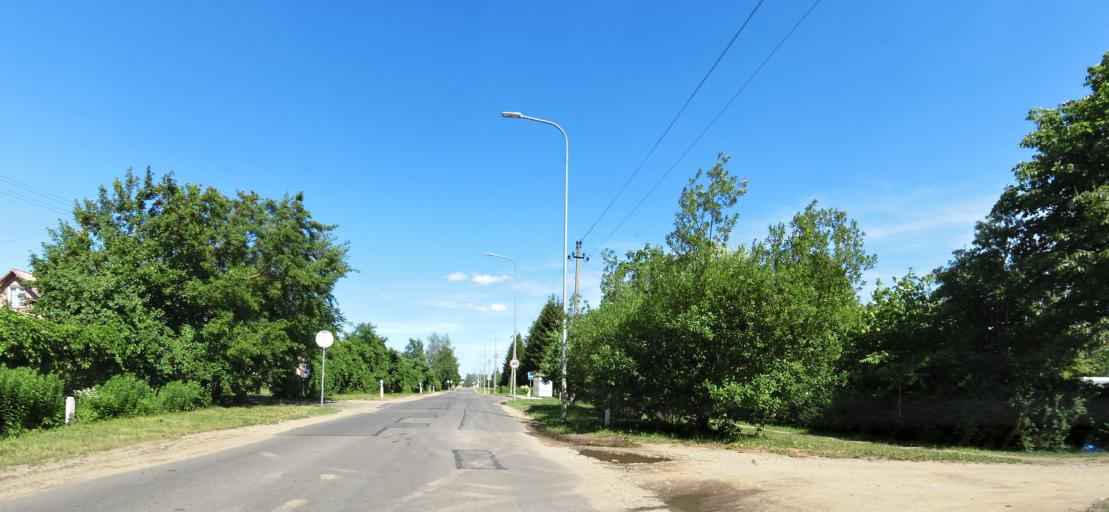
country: LT
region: Vilnius County
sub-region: Vilnius
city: Fabijoniskes
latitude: 54.8000
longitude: 25.3343
